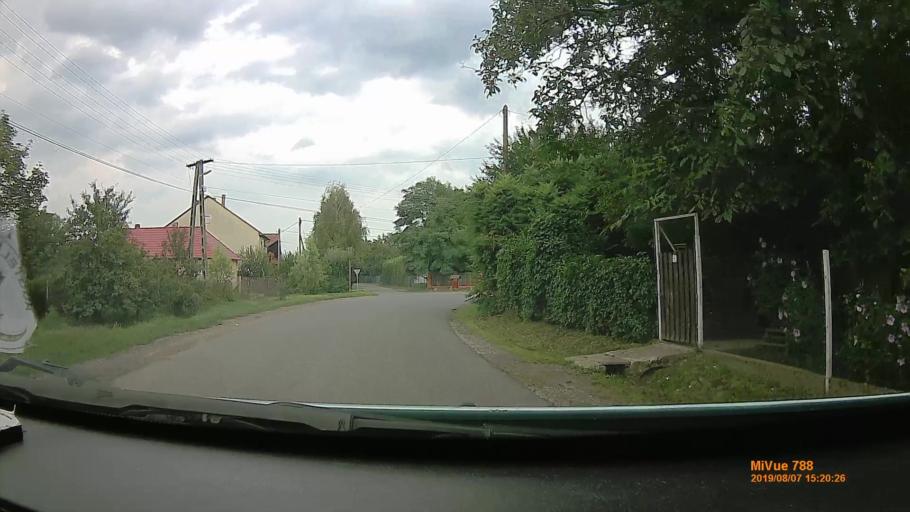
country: HU
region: Borsod-Abauj-Zemplen
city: Encs
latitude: 48.3558
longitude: 21.1480
